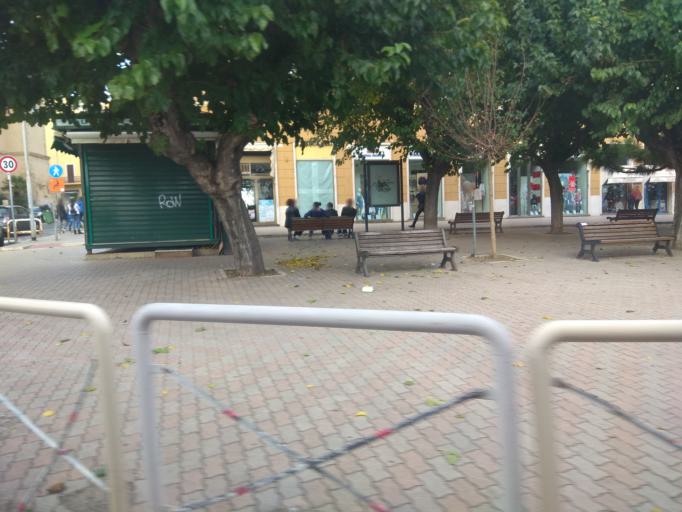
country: IT
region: Latium
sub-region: Citta metropolitana di Roma Capitale
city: Civitavecchia
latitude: 42.0904
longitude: 11.7924
